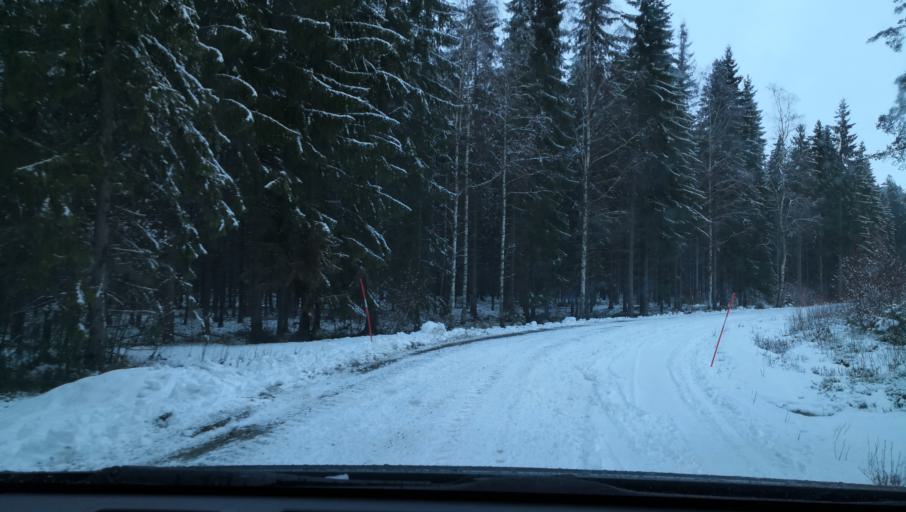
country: SE
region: Vaestmanland
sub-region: Kopings Kommun
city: Kolsva
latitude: 59.5590
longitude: 15.8538
